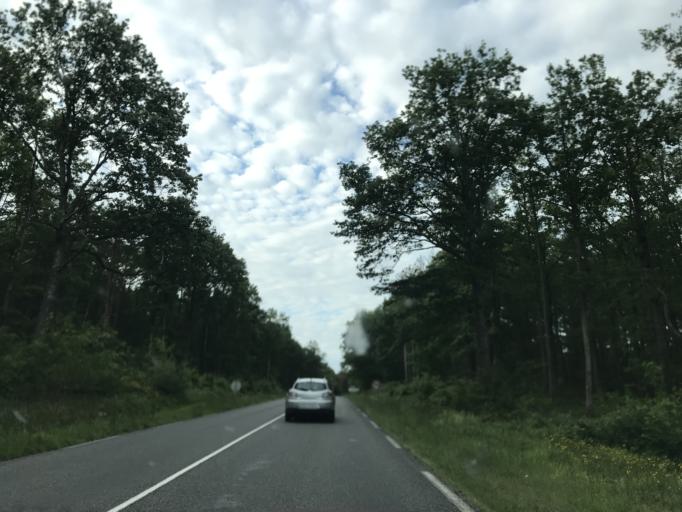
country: FR
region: Auvergne
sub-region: Departement de l'Allier
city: Brugheas
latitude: 46.0677
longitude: 3.3799
